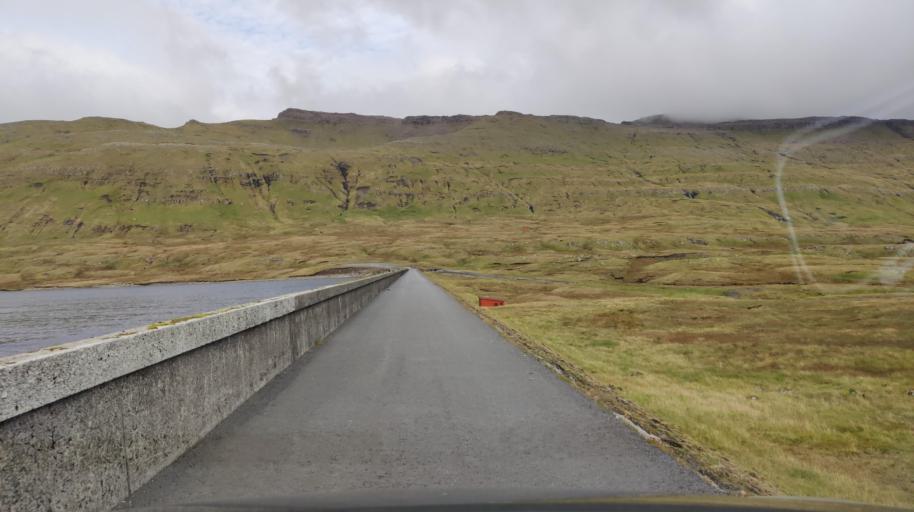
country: FO
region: Streymoy
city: Vestmanna
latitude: 62.1644
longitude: -7.0825
